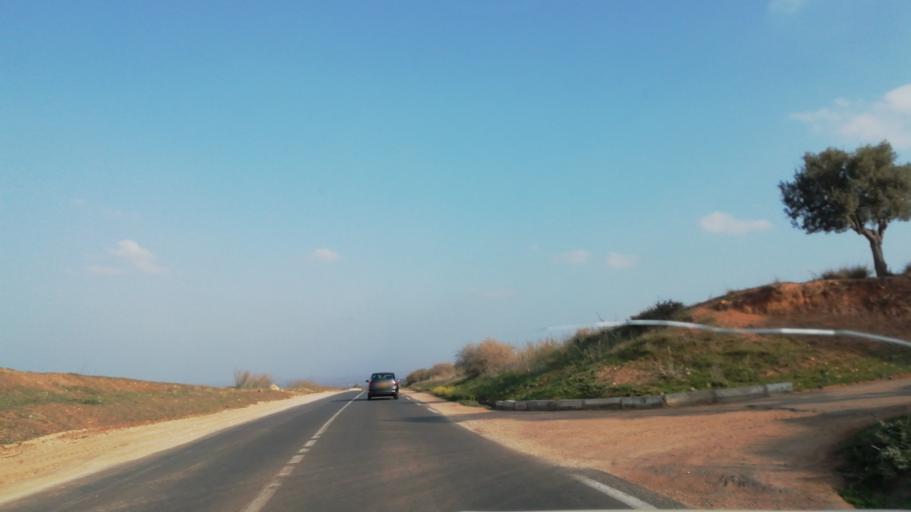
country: DZ
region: Ain Temouchent
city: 'Ain Temouchent
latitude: 35.3045
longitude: -1.0620
